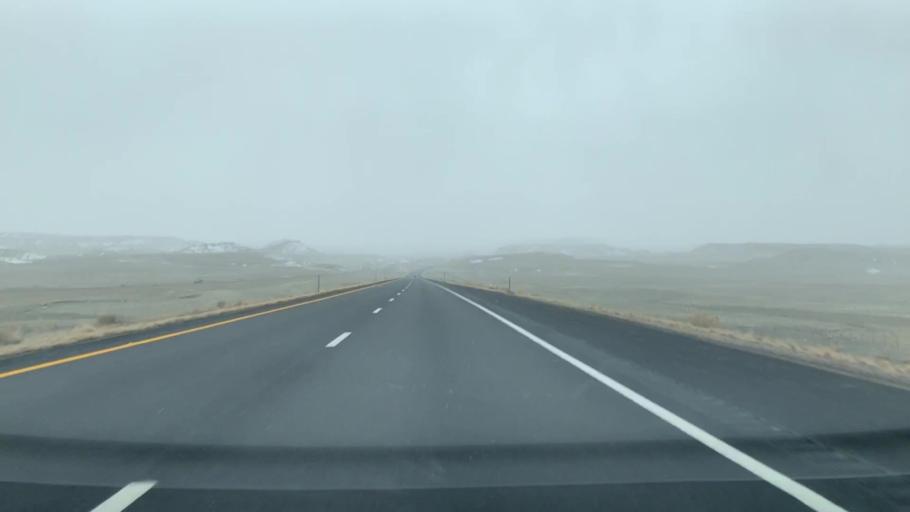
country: US
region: Utah
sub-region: Carbon County
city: East Carbon City
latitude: 38.9375
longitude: -110.3448
